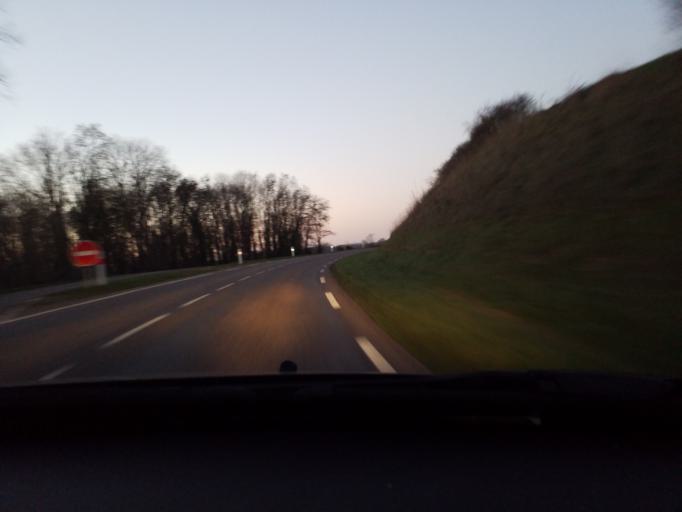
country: FR
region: Franche-Comte
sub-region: Departement de la Haute-Saone
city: Jussey
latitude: 47.9219
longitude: 5.9591
